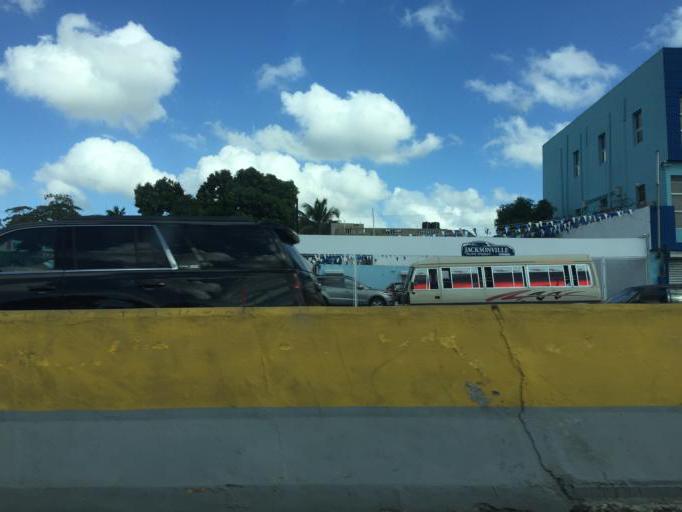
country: DO
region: Santo Domingo
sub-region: Santo Domingo
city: Santo Domingo Este
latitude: 18.4857
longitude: -69.8750
